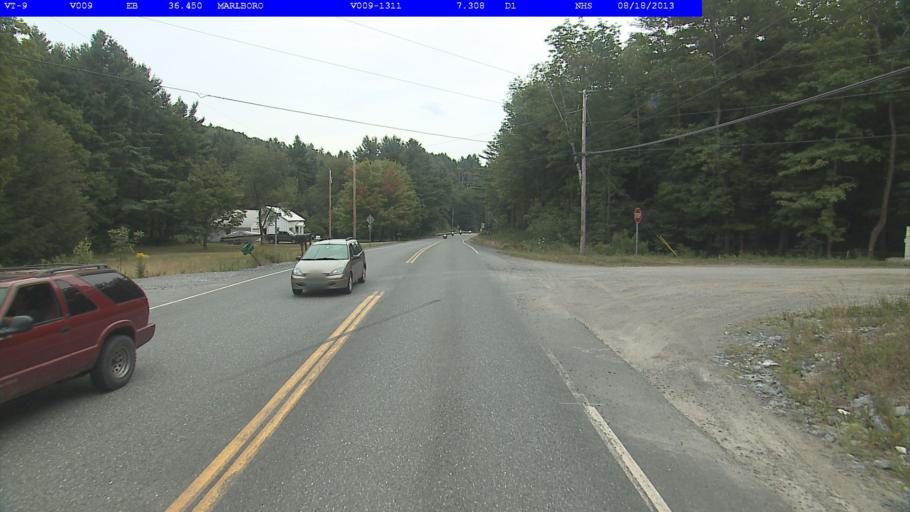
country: US
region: Vermont
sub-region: Windham County
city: West Brattleboro
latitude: 42.8782
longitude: -72.6947
